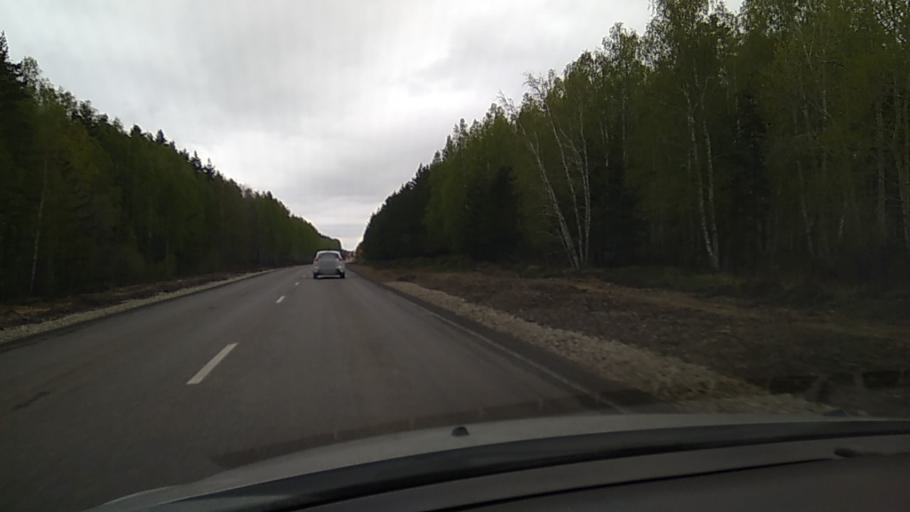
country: RU
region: Kurgan
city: Shadrinsk
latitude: 56.1424
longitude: 63.5121
